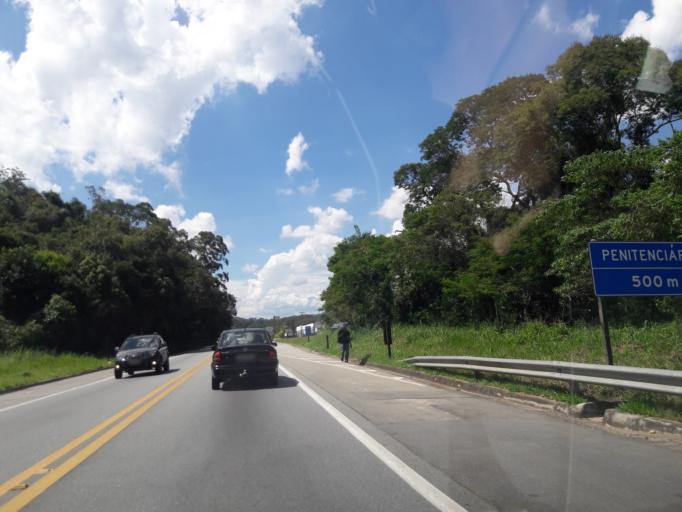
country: BR
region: Sao Paulo
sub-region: Francisco Morato
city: Francisco Morato
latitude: -23.3073
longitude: -46.8129
